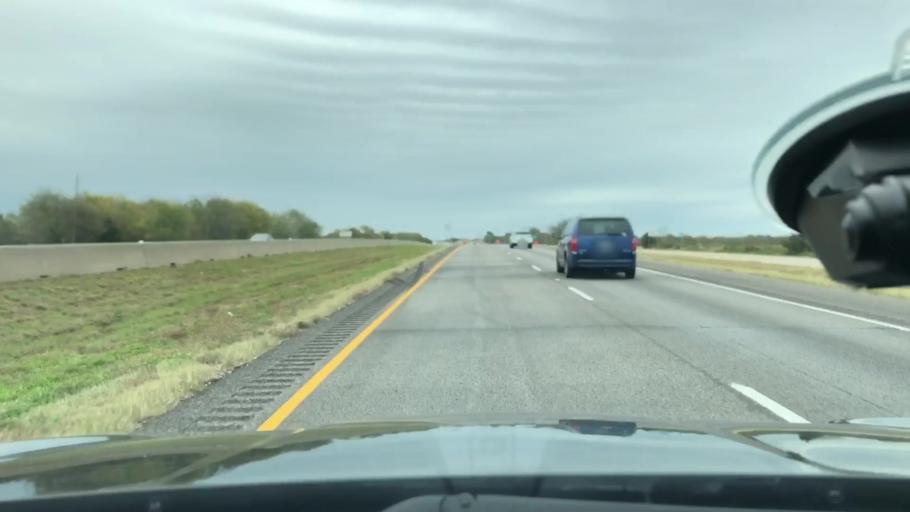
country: US
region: Texas
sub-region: Hunt County
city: Commerce
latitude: 33.1293
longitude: -95.8560
